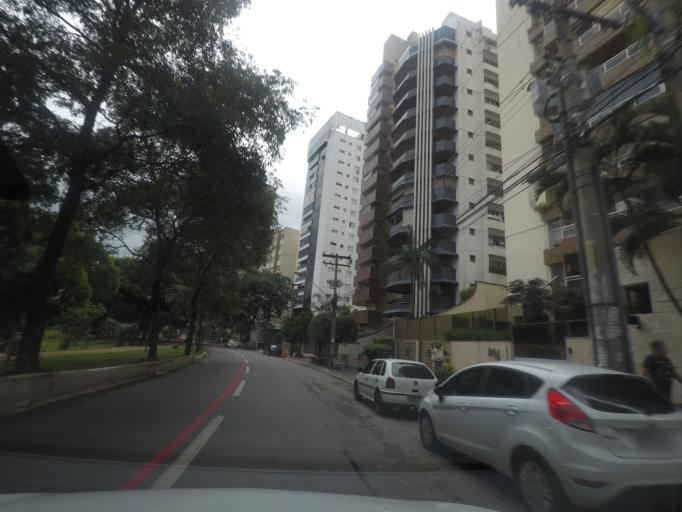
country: BR
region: Goias
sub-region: Goiania
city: Goiania
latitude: -16.6859
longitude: -49.2706
